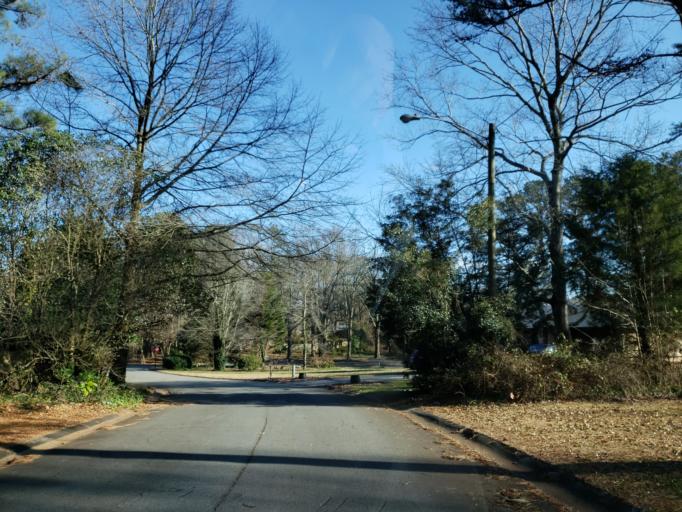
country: US
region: Georgia
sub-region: Cobb County
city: Marietta
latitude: 33.9919
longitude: -84.5205
